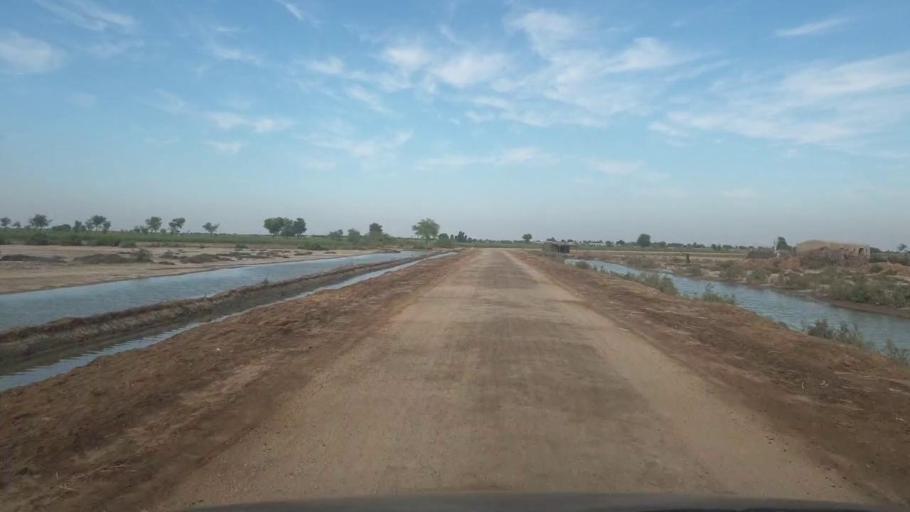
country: PK
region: Sindh
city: Mirwah Gorchani
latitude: 25.3718
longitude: 69.2093
